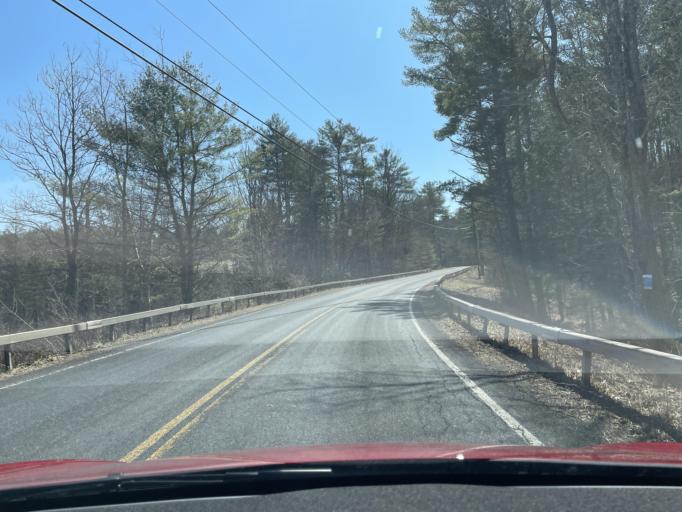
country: US
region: New York
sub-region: Ulster County
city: Shokan
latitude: 42.0233
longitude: -74.1925
